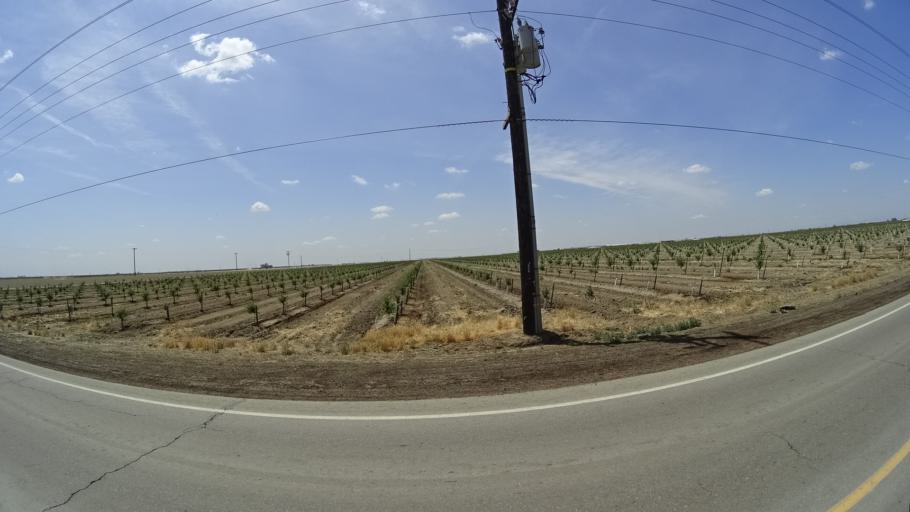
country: US
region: California
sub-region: Tulare County
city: Goshen
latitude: 36.2987
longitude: -119.5214
